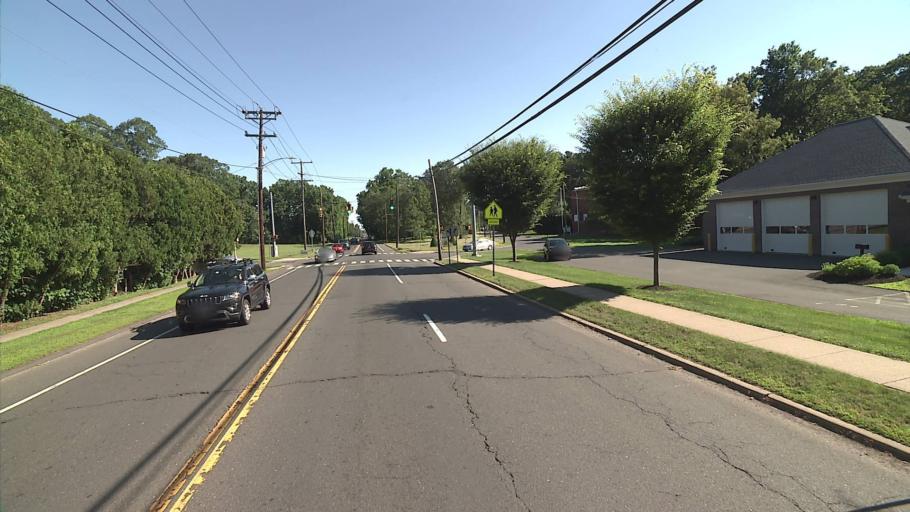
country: US
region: Connecticut
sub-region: New Haven County
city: Cheshire Village
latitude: 41.5167
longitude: -72.8980
